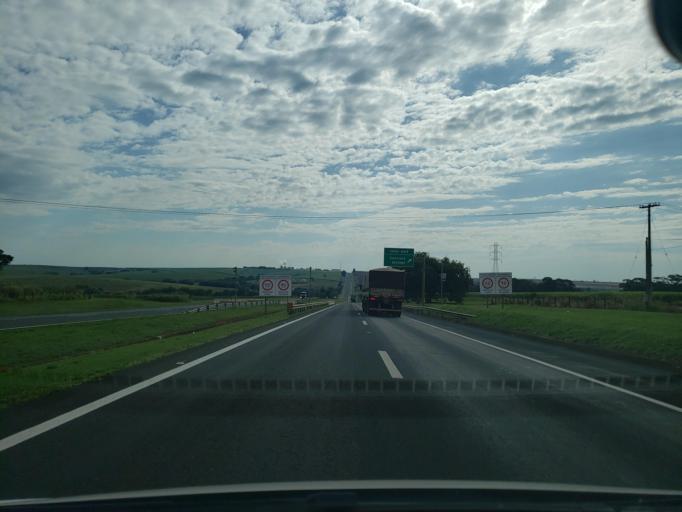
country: BR
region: Sao Paulo
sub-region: Lins
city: Lins
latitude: -21.6543
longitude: -49.8060
